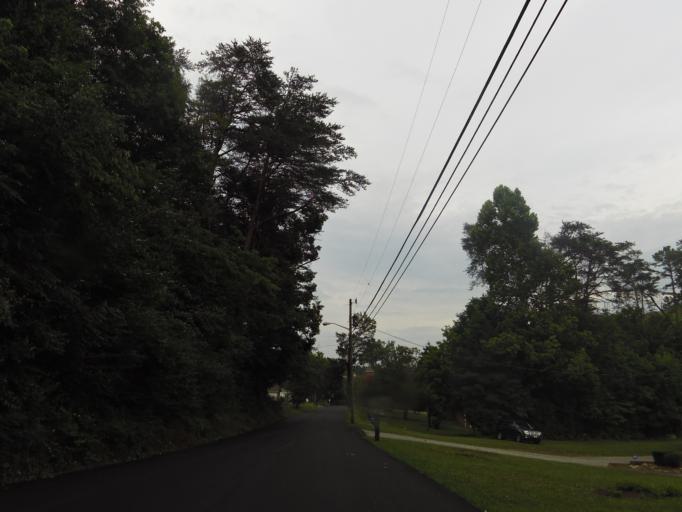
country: US
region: Tennessee
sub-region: Knox County
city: Knoxville
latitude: 36.0342
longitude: -83.9093
